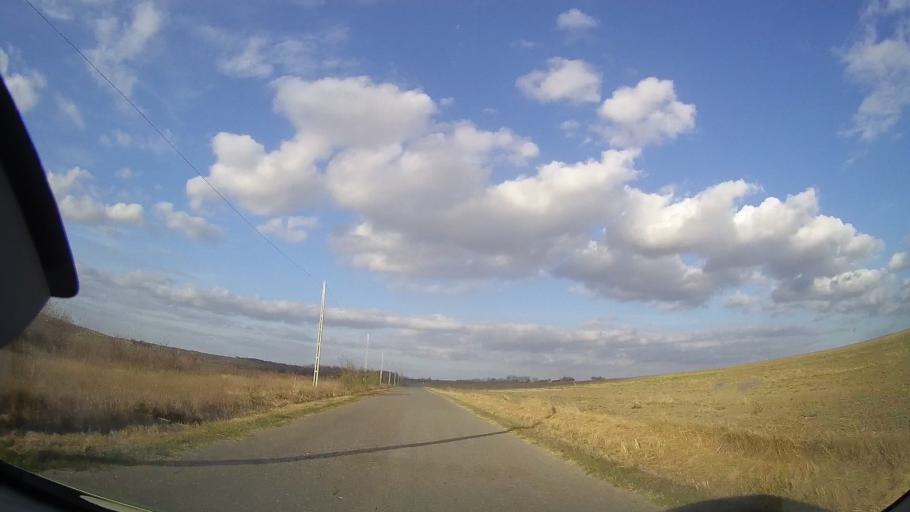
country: RO
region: Constanta
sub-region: Comuna Cerchezu
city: Cerchezu
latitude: 43.8481
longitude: 28.0993
